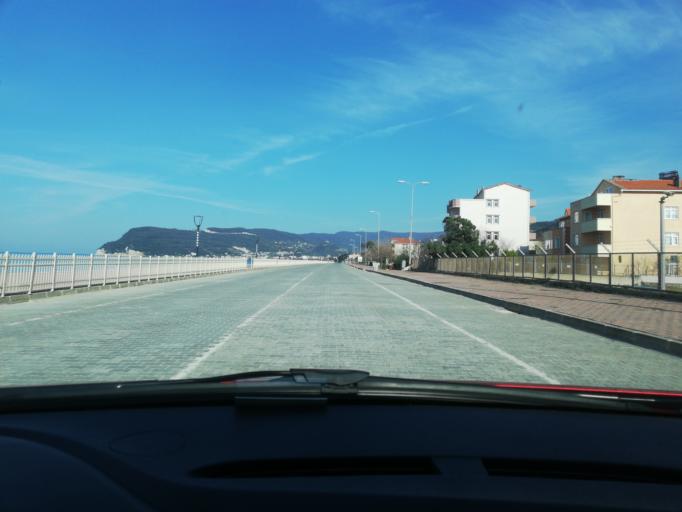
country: TR
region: Kastamonu
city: Cide
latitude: 41.8847
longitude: 32.9529
